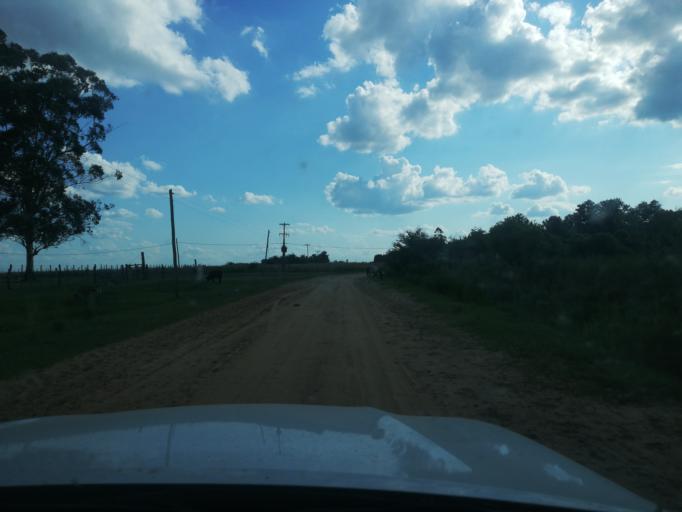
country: AR
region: Corrientes
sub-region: Departamento de San Miguel
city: San Miguel
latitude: -27.9972
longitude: -57.5799
